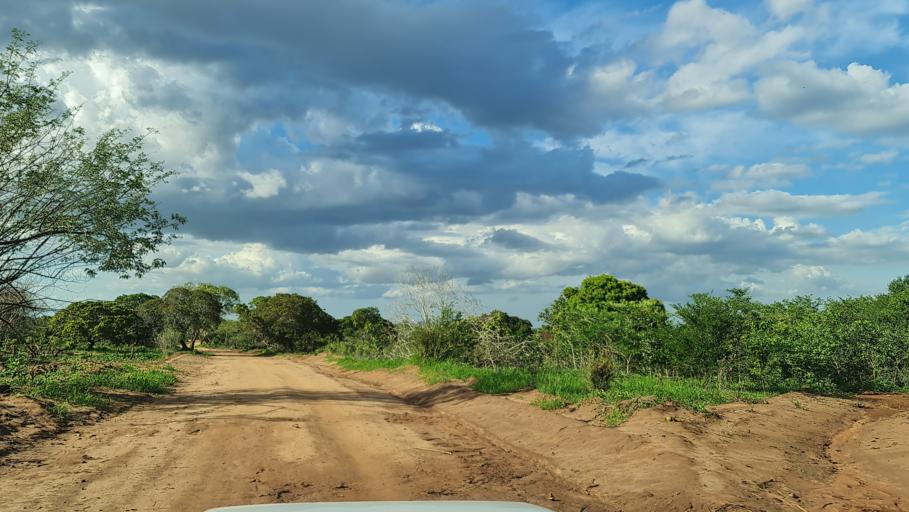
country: MZ
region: Cabo Delgado
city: Pemba
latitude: -13.5515
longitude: 40.1031
